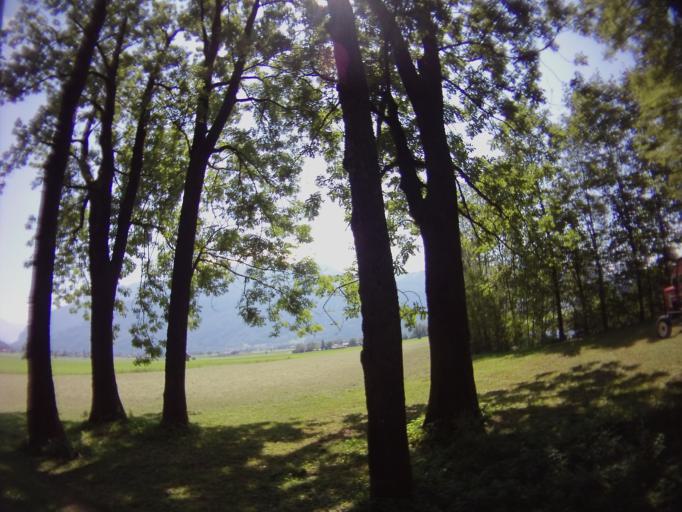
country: CH
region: Saint Gallen
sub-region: Wahlkreis See-Gaster
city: Schanis
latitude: 47.1762
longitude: 9.0473
